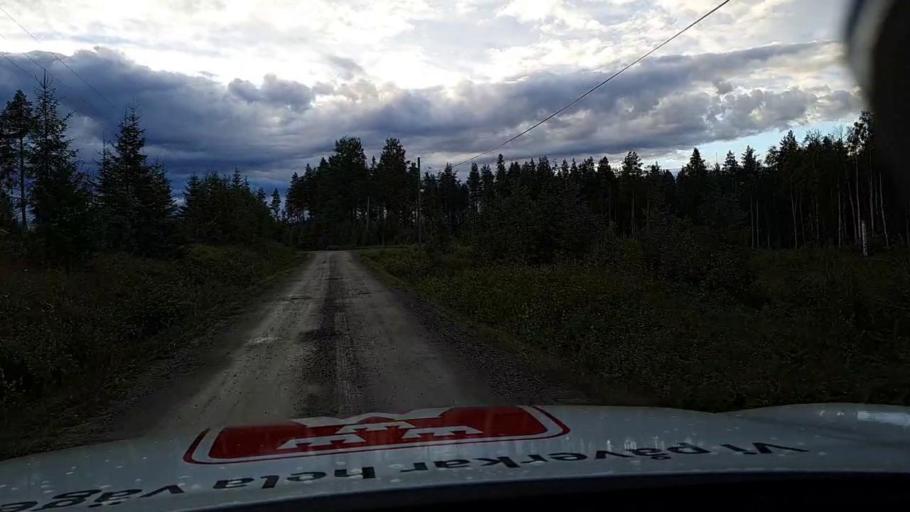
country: SE
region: Jaemtland
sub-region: Bergs Kommun
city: Hoverberg
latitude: 62.8818
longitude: 14.5944
